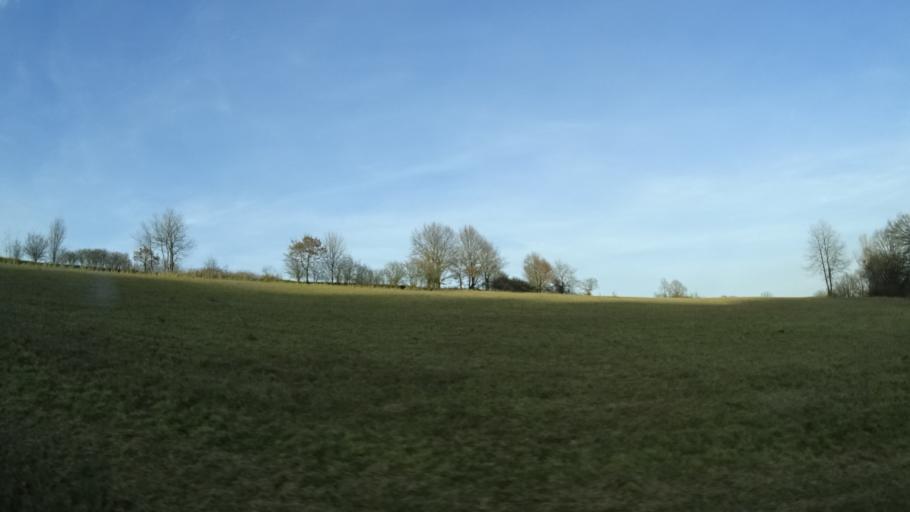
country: DE
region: Bavaria
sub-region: Regierungsbezirk Unterfranken
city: Zeitlofs
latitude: 50.3031
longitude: 9.6457
